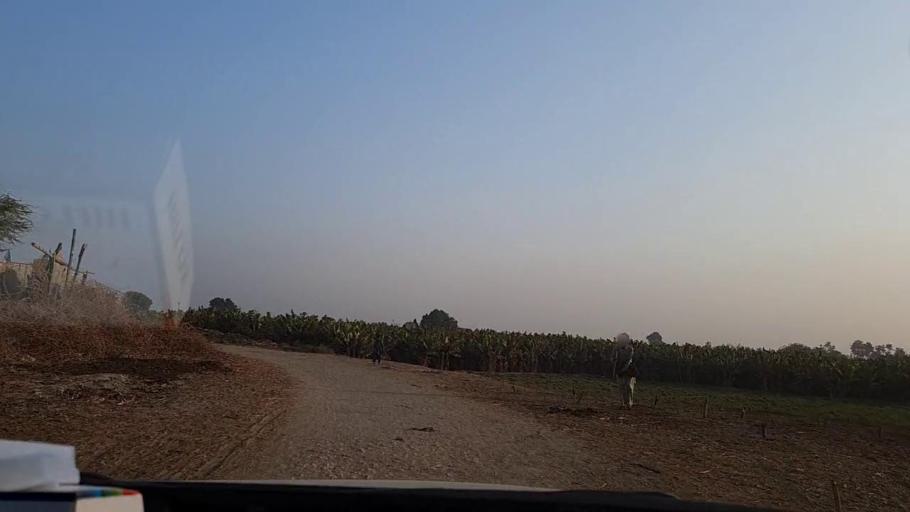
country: PK
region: Sindh
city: Tando Ghulam Ali
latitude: 25.1870
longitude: 68.9112
